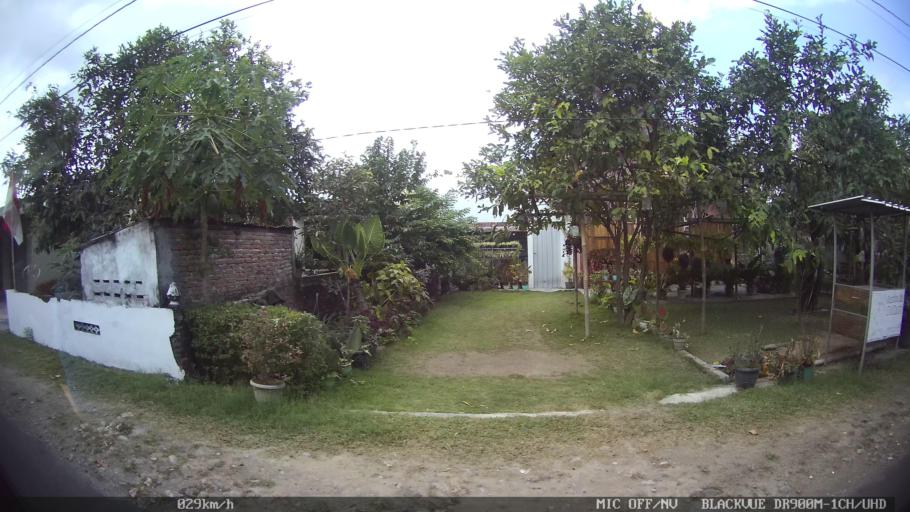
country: ID
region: Daerah Istimewa Yogyakarta
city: Depok
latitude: -7.8203
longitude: 110.4645
